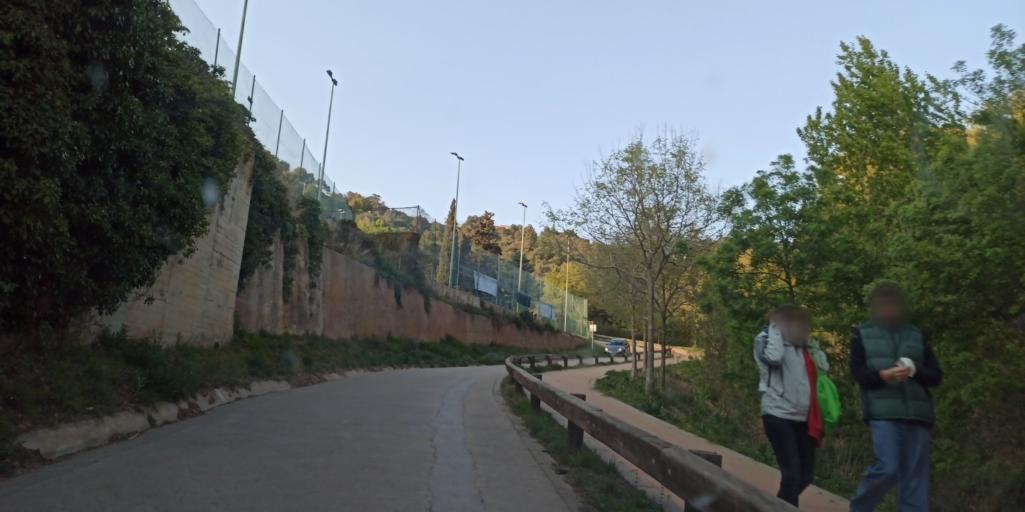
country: ES
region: Catalonia
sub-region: Provincia de Barcelona
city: Sant Just Desvern
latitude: 41.4034
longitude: 2.0872
